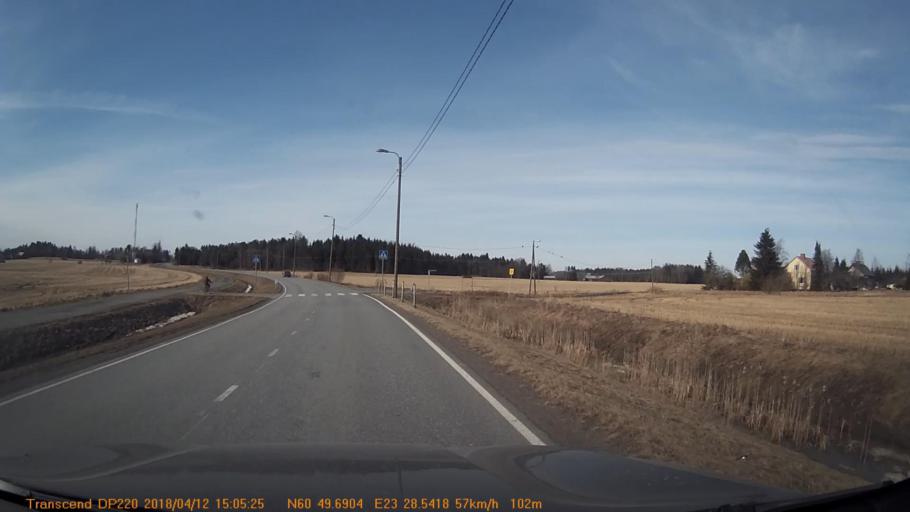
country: FI
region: Haeme
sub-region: Forssa
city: Jokioinen
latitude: 60.8283
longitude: 23.4756
